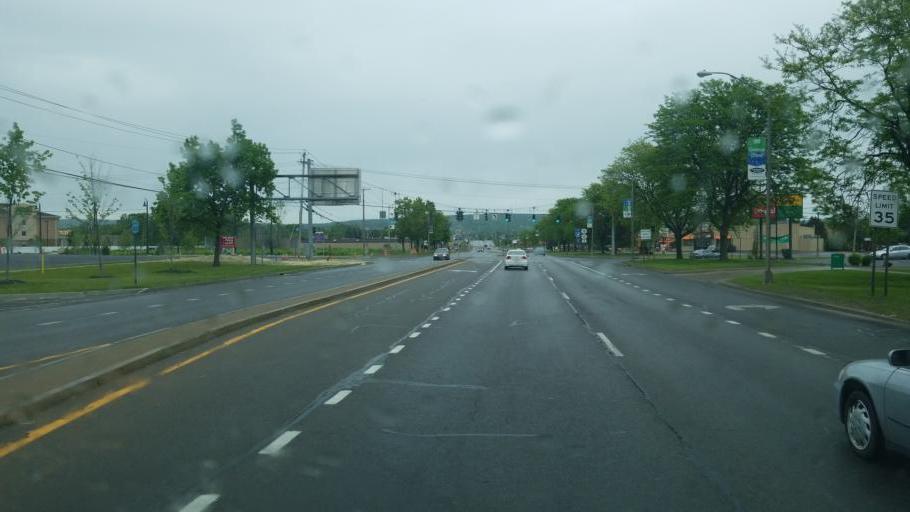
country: US
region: New York
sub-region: Oneida County
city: Utica
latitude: 43.1071
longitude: -75.2217
